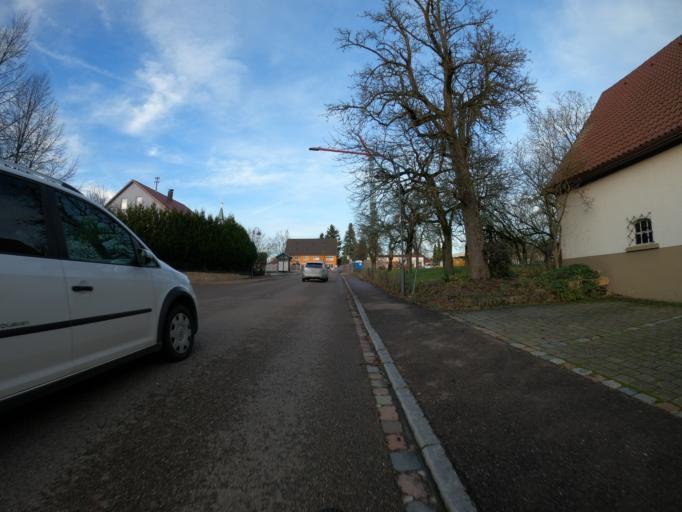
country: DE
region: Baden-Wuerttemberg
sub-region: Regierungsbezirk Stuttgart
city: Zell unter Aichelberg
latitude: 48.6511
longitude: 9.5713
